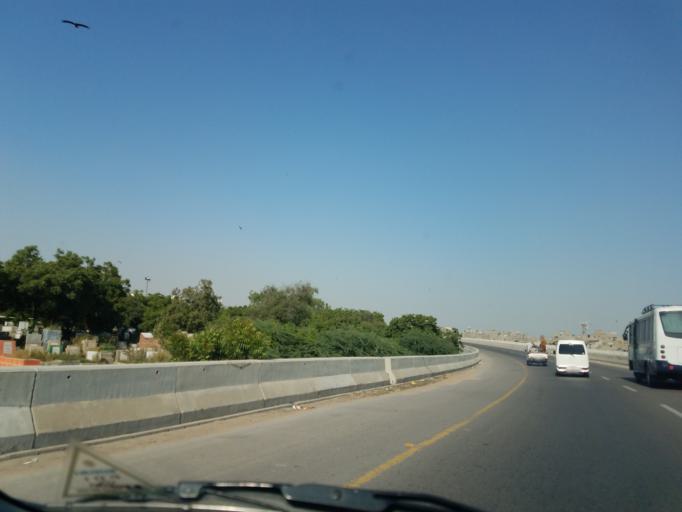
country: PK
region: Sindh
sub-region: Karachi District
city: Karachi
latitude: 24.9138
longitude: 67.0766
